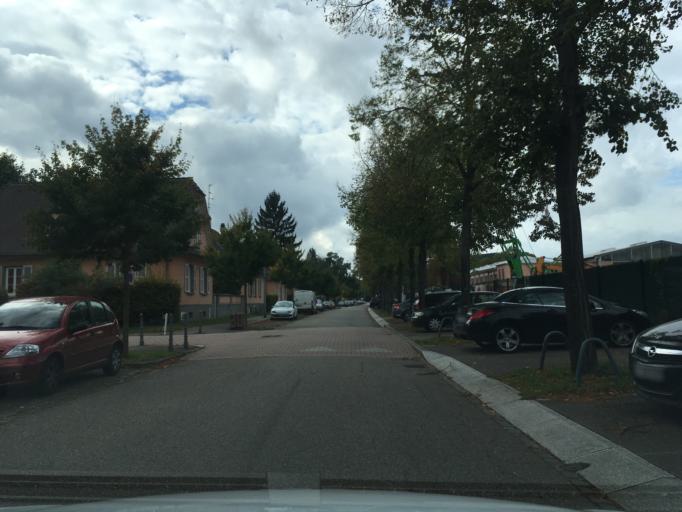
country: FR
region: Alsace
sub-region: Departement du Bas-Rhin
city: Schiltigheim
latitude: 48.5980
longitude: 7.7653
